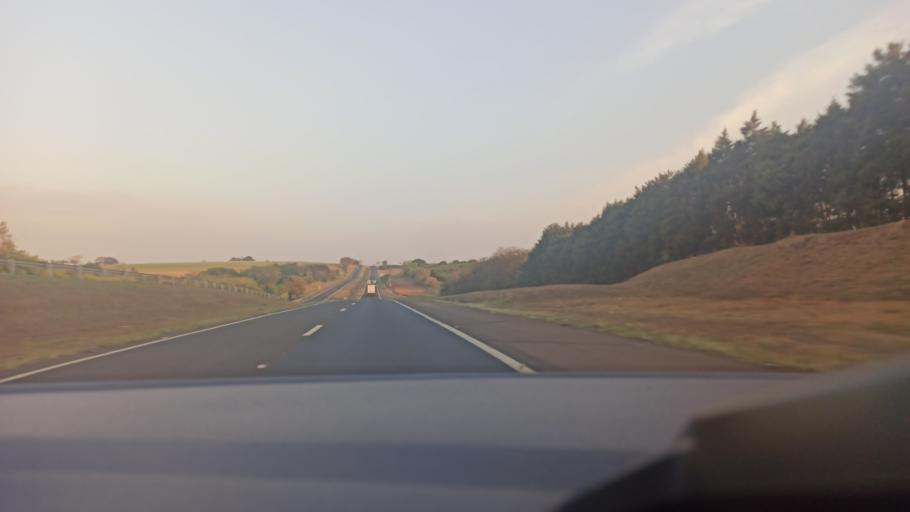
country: BR
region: Sao Paulo
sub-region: Santa Adelia
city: Santa Adelia
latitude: -21.3956
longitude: -48.7143
